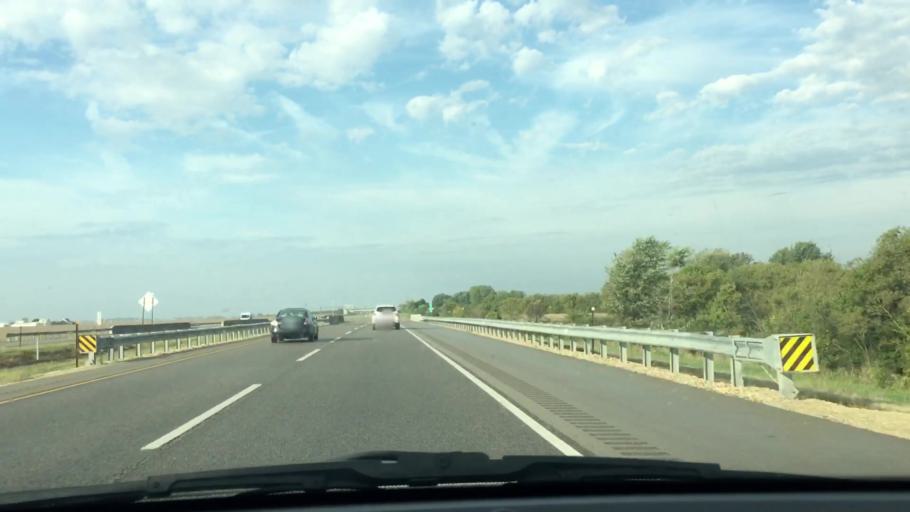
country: US
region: Illinois
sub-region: Ogle County
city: Rochelle
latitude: 41.8892
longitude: -89.0997
